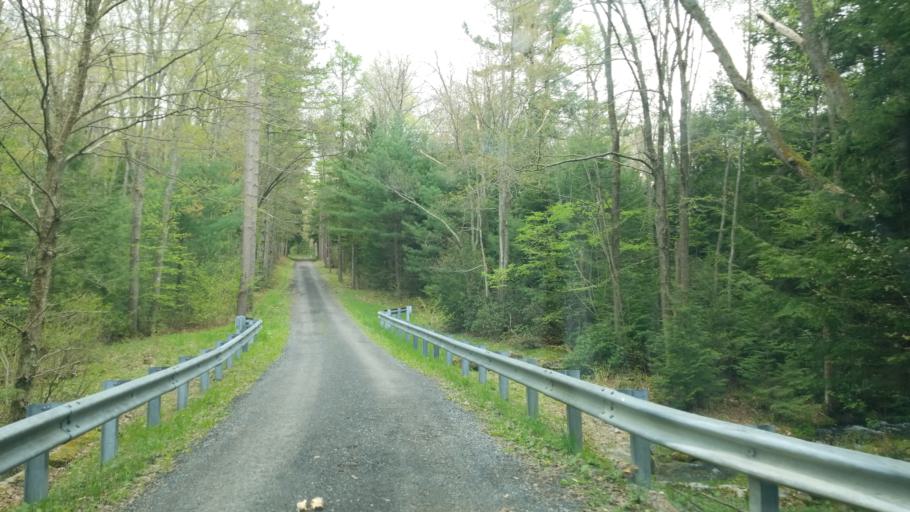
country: US
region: Pennsylvania
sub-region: Clearfield County
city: Shiloh
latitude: 41.2078
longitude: -78.1511
